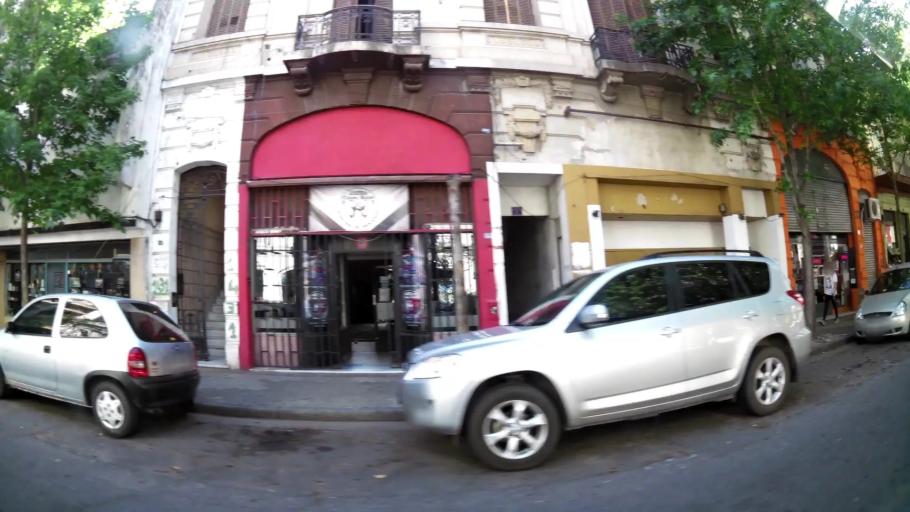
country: AR
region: Santa Fe
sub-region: Departamento de Rosario
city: Rosario
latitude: -32.9548
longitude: -60.6387
